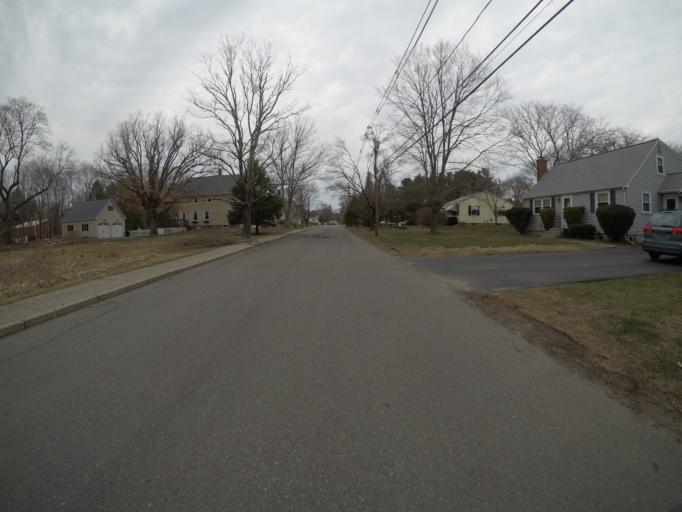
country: US
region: Massachusetts
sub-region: Bristol County
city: Easton
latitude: 42.0580
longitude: -71.0995
